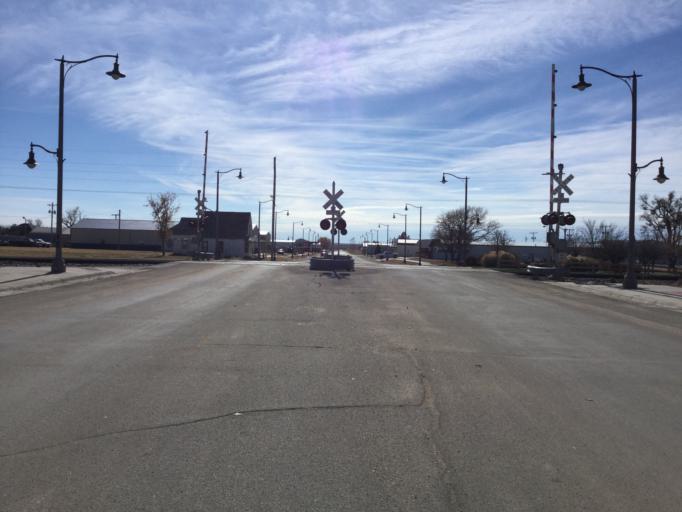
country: US
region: Kansas
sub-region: Trego County
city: WaKeeney
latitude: 39.0238
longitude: -99.8840
